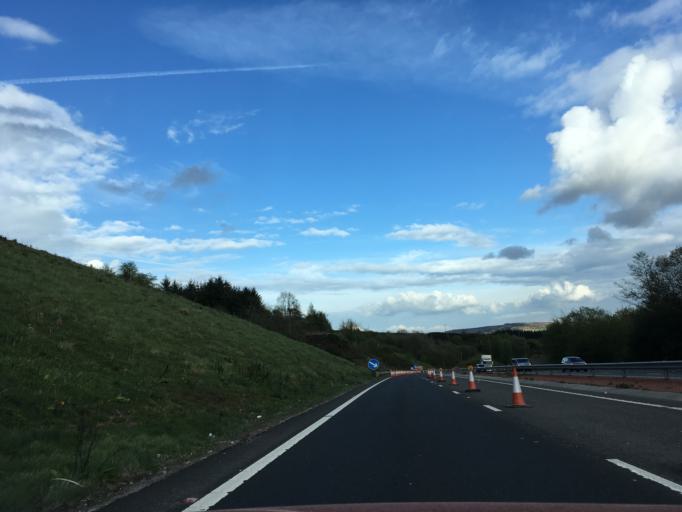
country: GB
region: Wales
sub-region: Blaenau Gwent
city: Brynmawr
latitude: 51.8092
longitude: -3.1782
